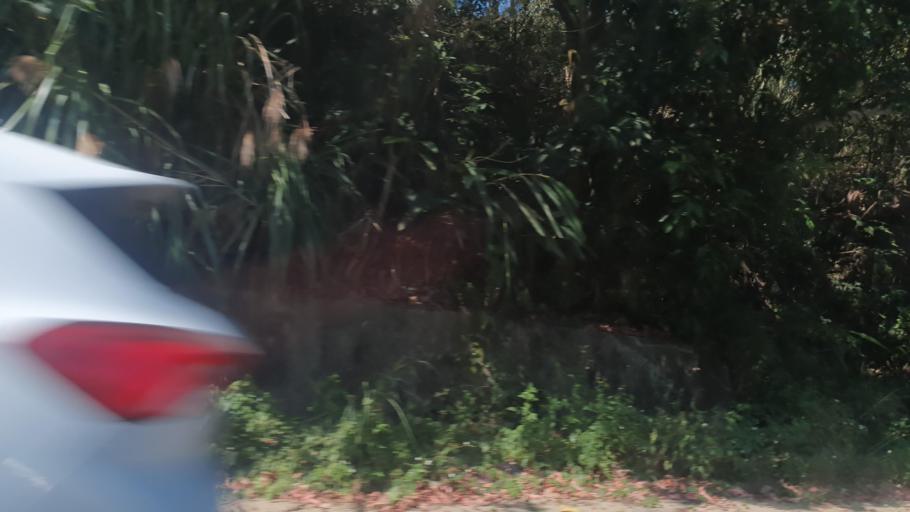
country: TW
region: Taiwan
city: Yujing
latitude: 23.0546
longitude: 120.3788
